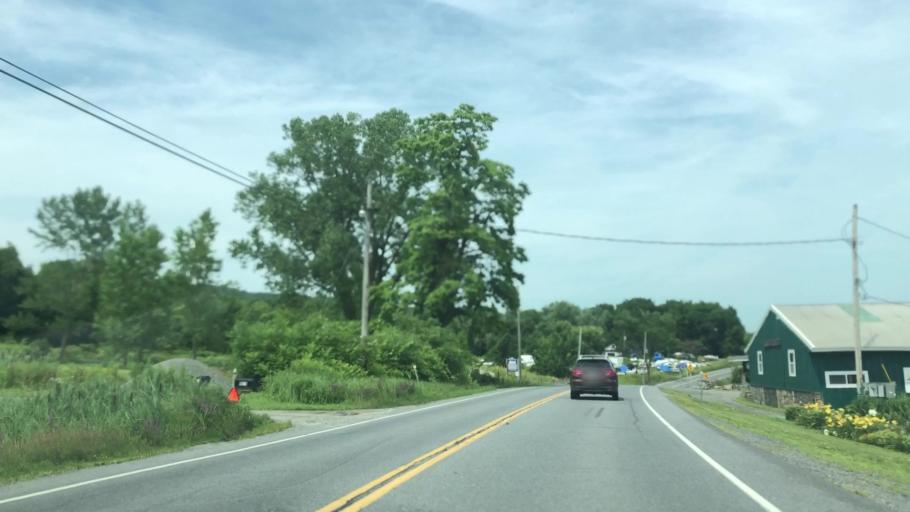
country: US
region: New York
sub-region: Washington County
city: Whitehall
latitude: 43.4834
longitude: -73.4313
